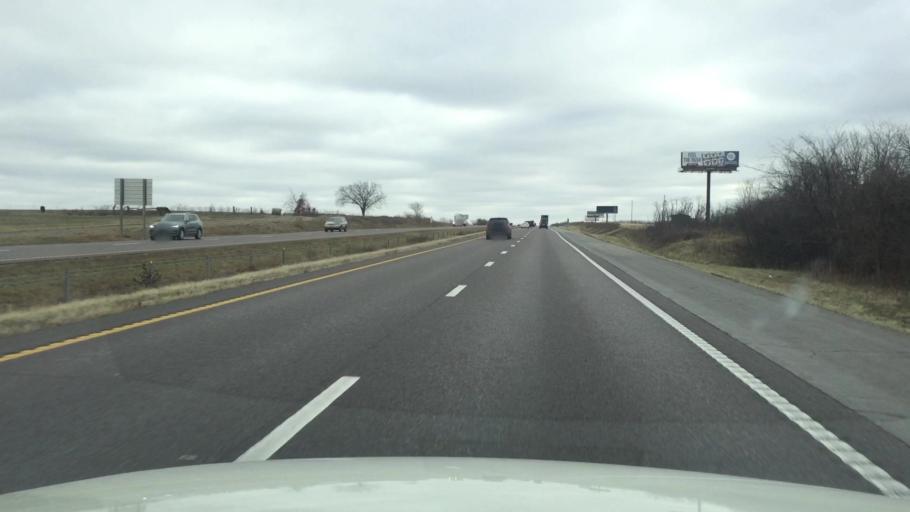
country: US
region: Missouri
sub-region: Saline County
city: Marshall
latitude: 38.9590
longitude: -93.1825
